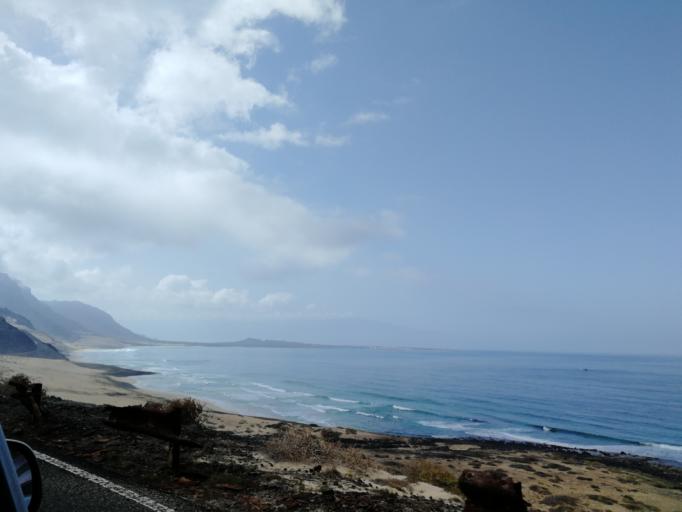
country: CV
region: Sao Vicente
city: Mindelo
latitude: 16.8613
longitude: -24.8875
